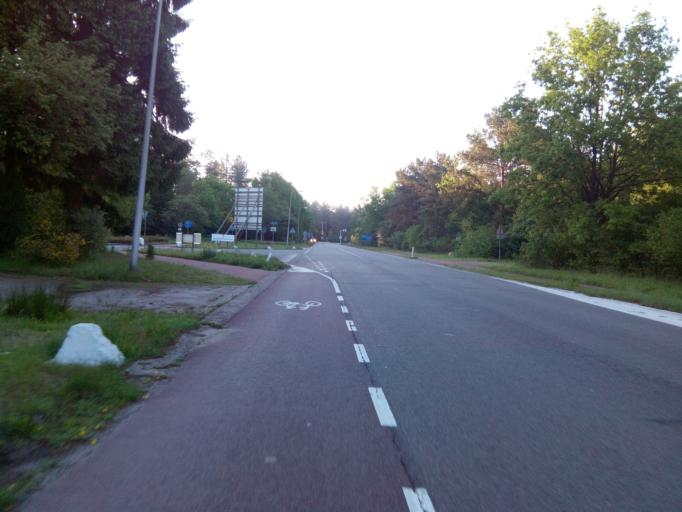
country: NL
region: Utrecht
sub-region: Gemeente Amersfoort
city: Amersfoort
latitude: 52.1217
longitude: 5.3590
